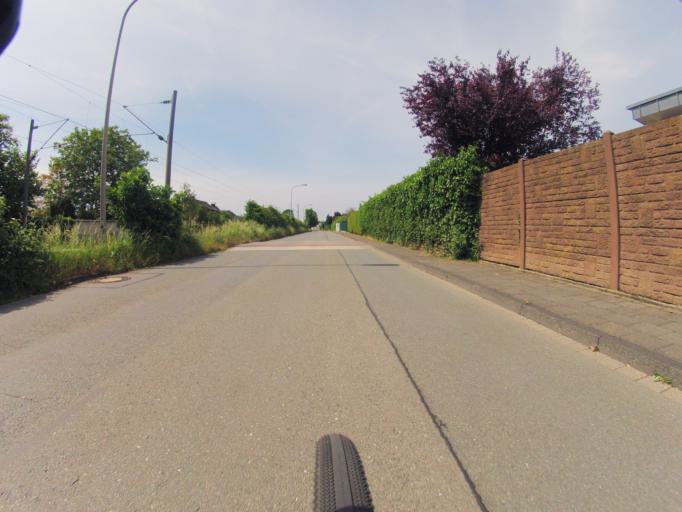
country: DE
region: North Rhine-Westphalia
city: Ibbenburen
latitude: 52.2839
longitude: 7.7093
